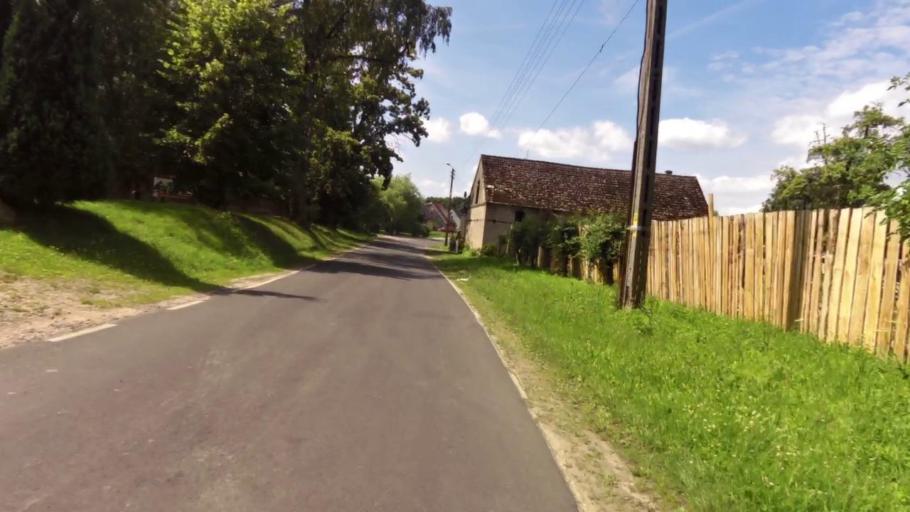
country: PL
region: West Pomeranian Voivodeship
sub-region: Powiat stargardzki
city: Insko
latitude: 53.4250
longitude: 15.4785
